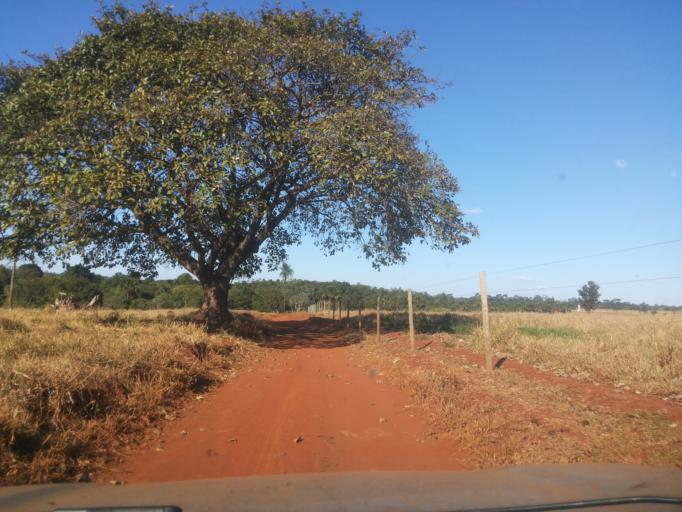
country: BR
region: Minas Gerais
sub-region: Centralina
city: Centralina
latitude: -18.7399
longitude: -49.1619
